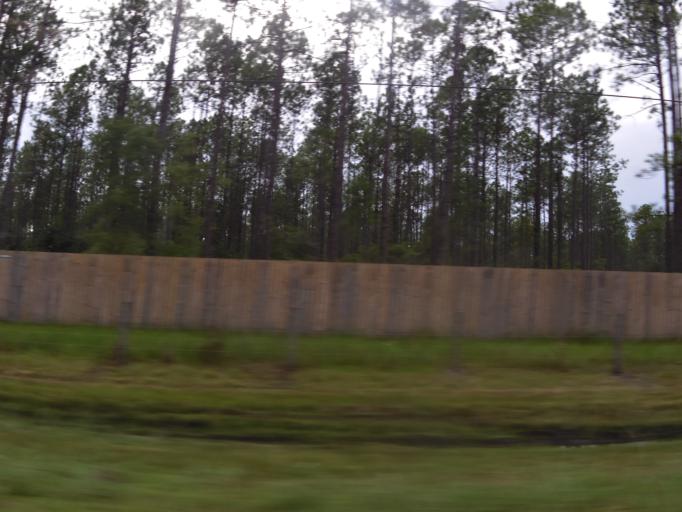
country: US
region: Florida
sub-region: Duval County
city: Baldwin
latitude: 30.3476
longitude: -81.9108
